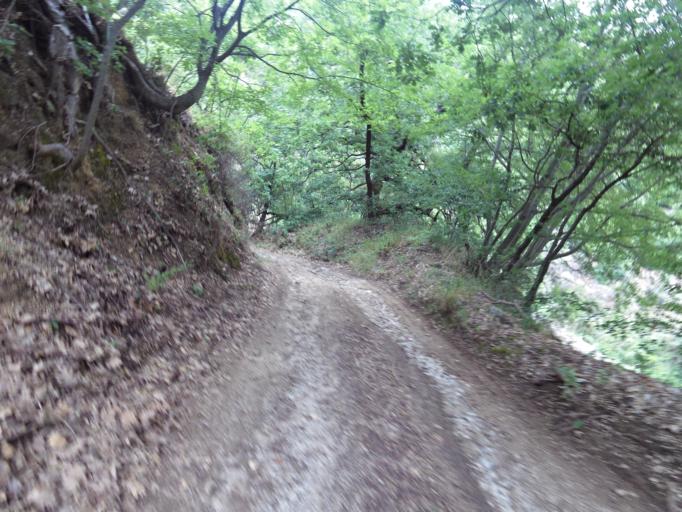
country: IT
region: Calabria
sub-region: Provincia di Reggio Calabria
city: Bivongi
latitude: 38.4902
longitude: 16.4286
